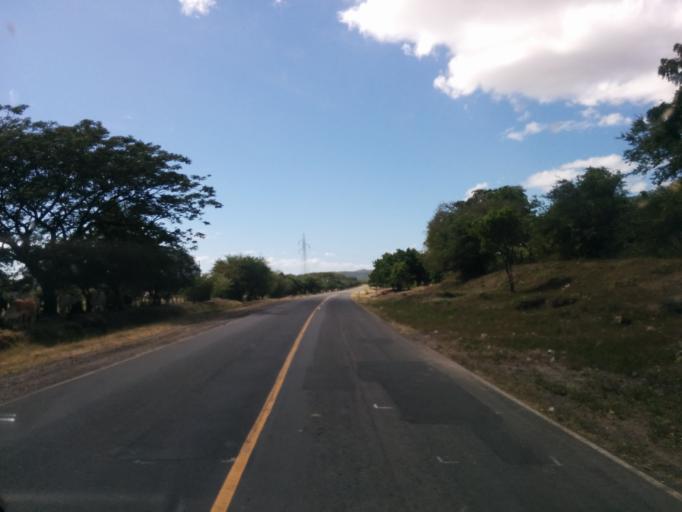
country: NI
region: Matagalpa
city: Ciudad Dario
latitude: 12.8345
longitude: -86.2189
